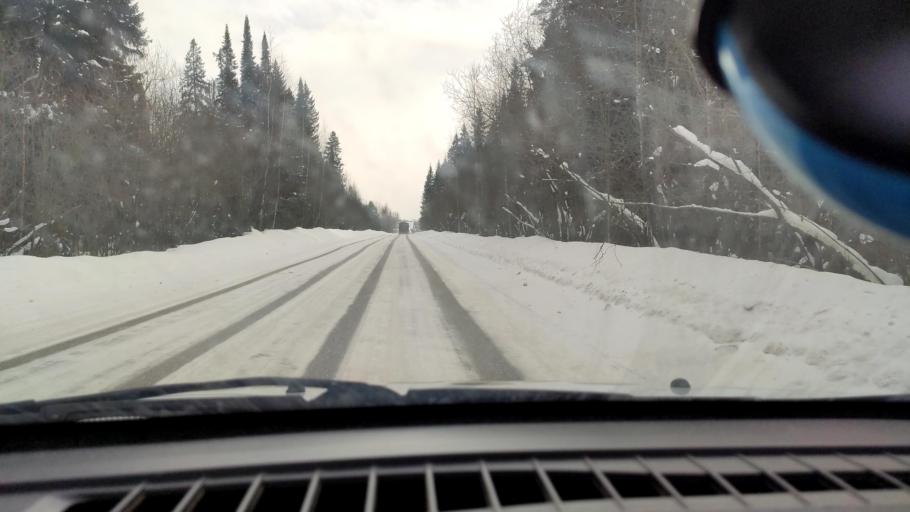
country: RU
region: Perm
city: Overyata
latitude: 58.1028
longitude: 55.8433
